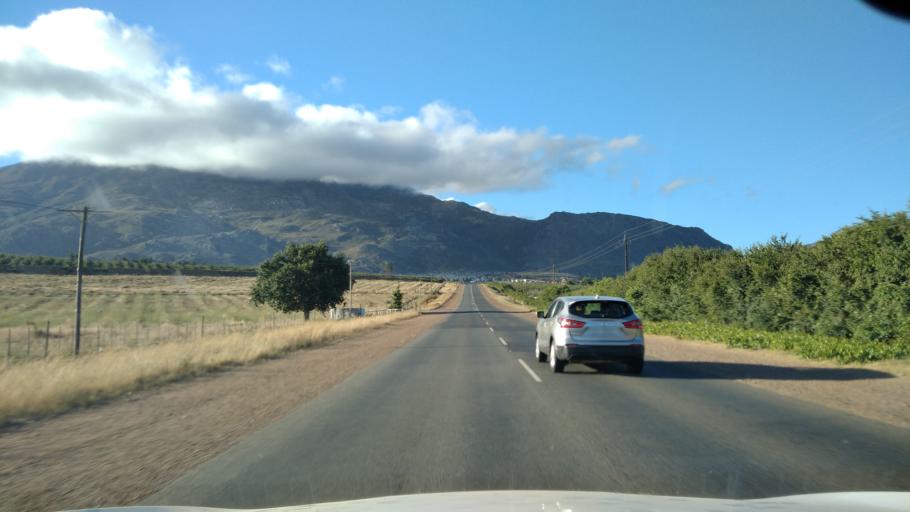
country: ZA
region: Western Cape
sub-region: Overberg District Municipality
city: Caledon
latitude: -34.0049
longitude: 19.2908
